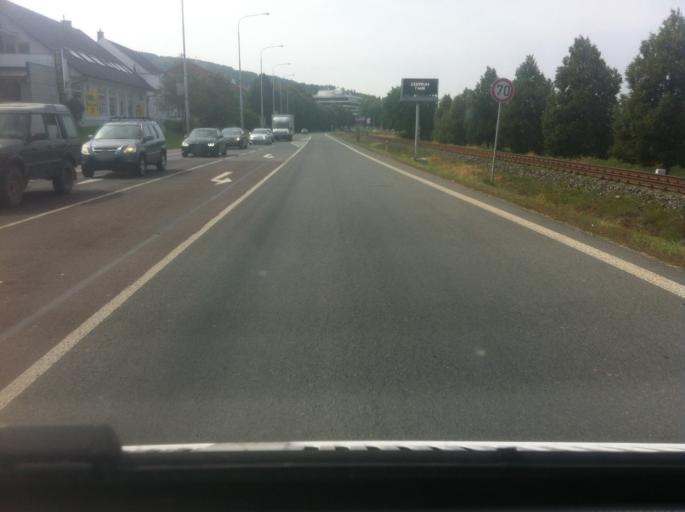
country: CZ
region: Zlin
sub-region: Okres Zlin
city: Zlin
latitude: 49.2208
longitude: 17.7148
